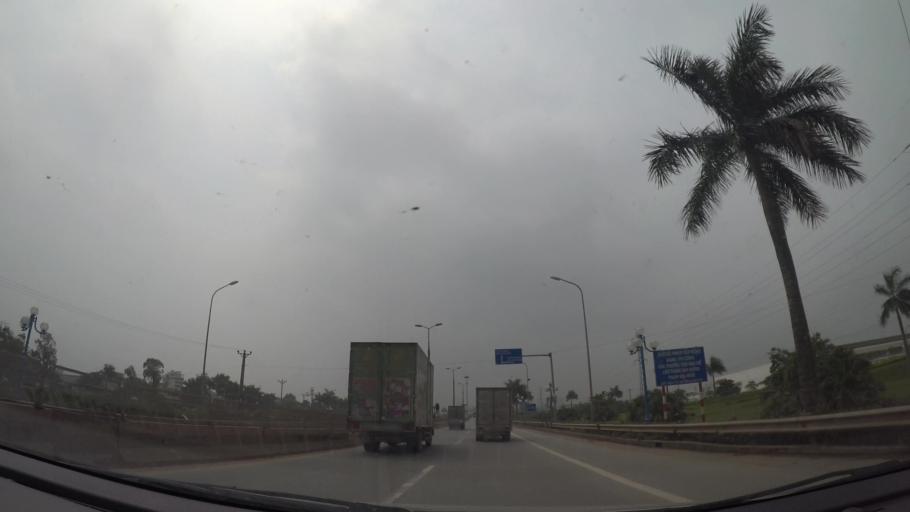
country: VN
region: Ha Noi
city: Tay Ho
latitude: 21.1158
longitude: 105.7845
